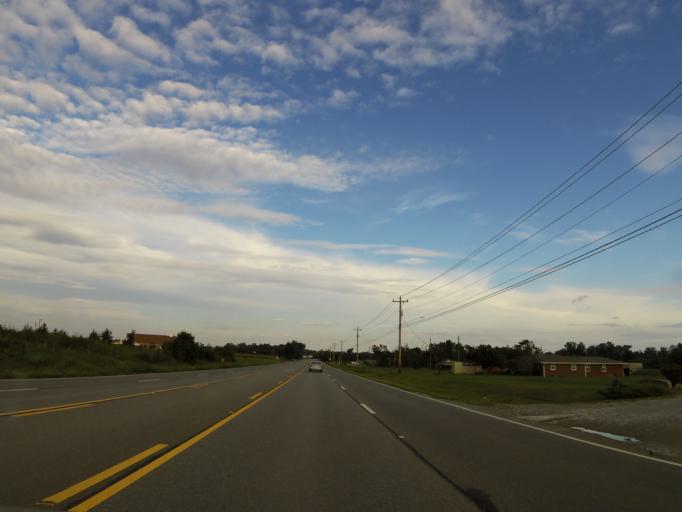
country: US
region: Alabama
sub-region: Lauderdale County
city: Rogersville
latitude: 34.7987
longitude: -87.1369
